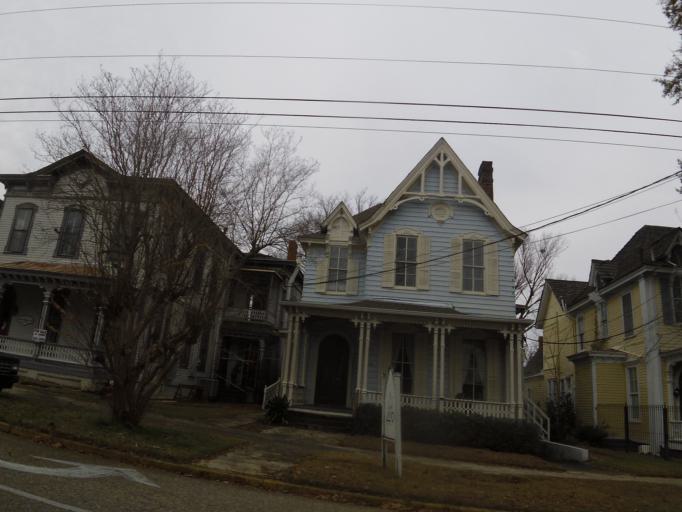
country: US
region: Alabama
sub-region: Montgomery County
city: Montgomery
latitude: 32.3733
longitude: -86.3073
